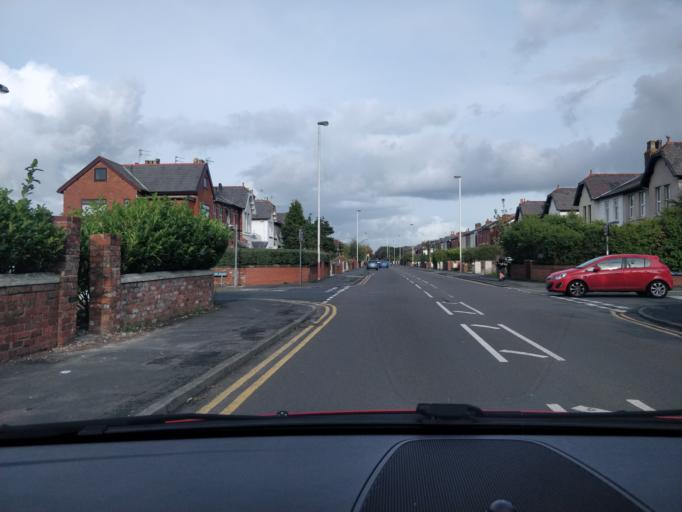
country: GB
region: England
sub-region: Sefton
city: Southport
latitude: 53.6328
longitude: -3.0045
